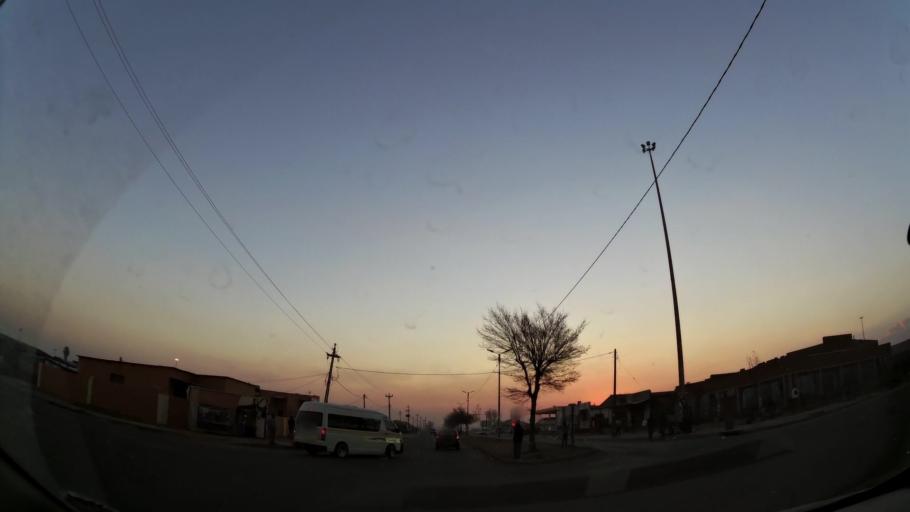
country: ZA
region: Gauteng
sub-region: Ekurhuleni Metropolitan Municipality
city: Nigel
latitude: -26.3753
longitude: 28.4094
